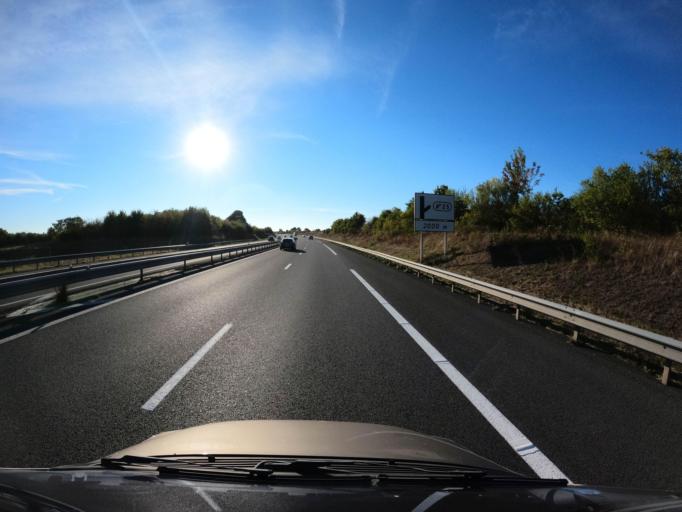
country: FR
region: Pays de la Loire
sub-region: Departement de Maine-et-Loire
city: Chemille-Melay
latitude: 47.2477
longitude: -0.7014
